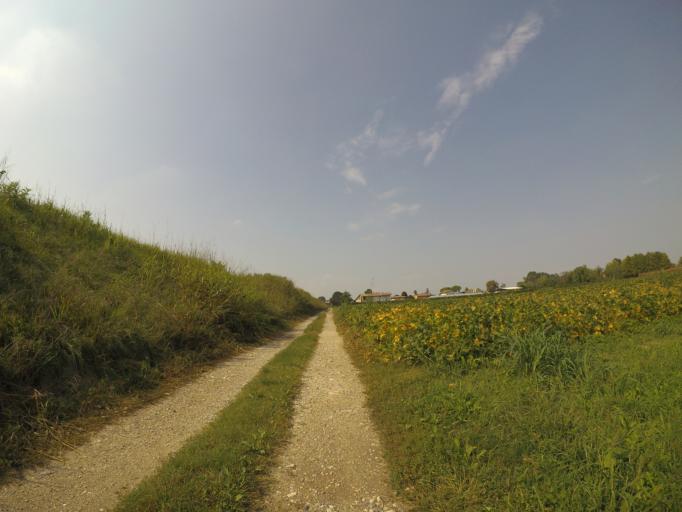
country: IT
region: Friuli Venezia Giulia
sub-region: Provincia di Udine
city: Varmo
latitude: 45.8884
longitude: 12.9621
